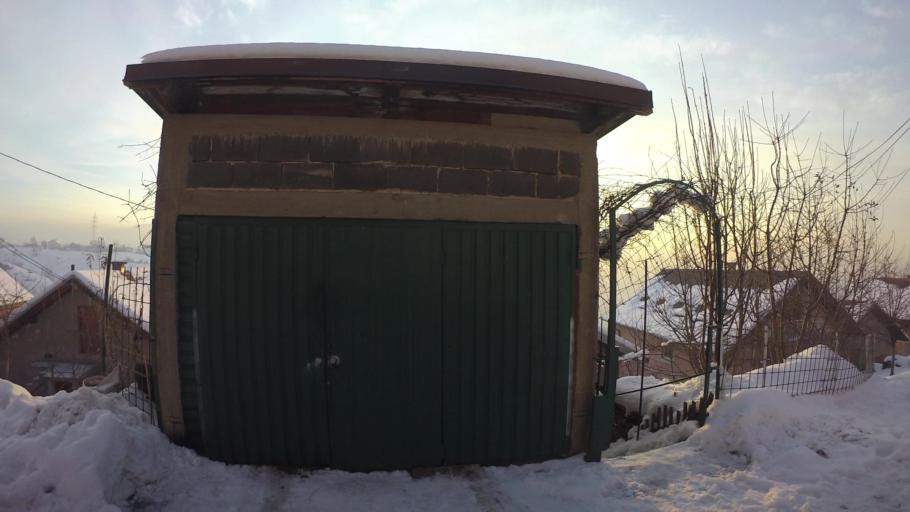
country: BA
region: Federation of Bosnia and Herzegovina
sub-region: Kanton Sarajevo
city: Sarajevo
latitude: 43.8391
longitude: 18.3560
